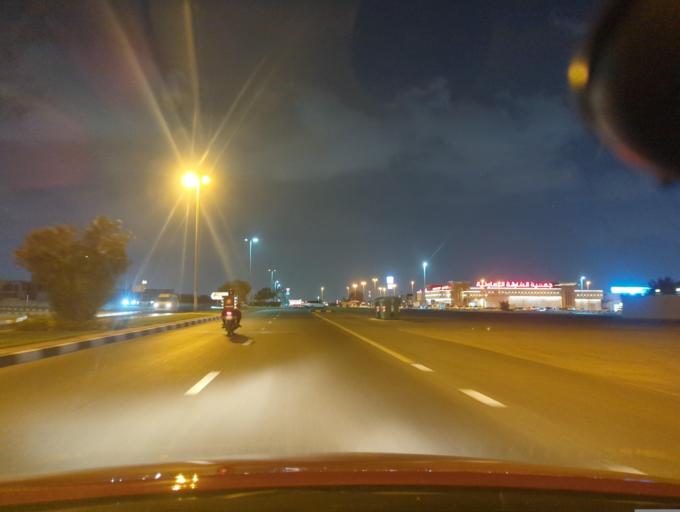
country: AE
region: Ash Shariqah
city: Sharjah
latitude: 25.3496
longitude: 55.4633
